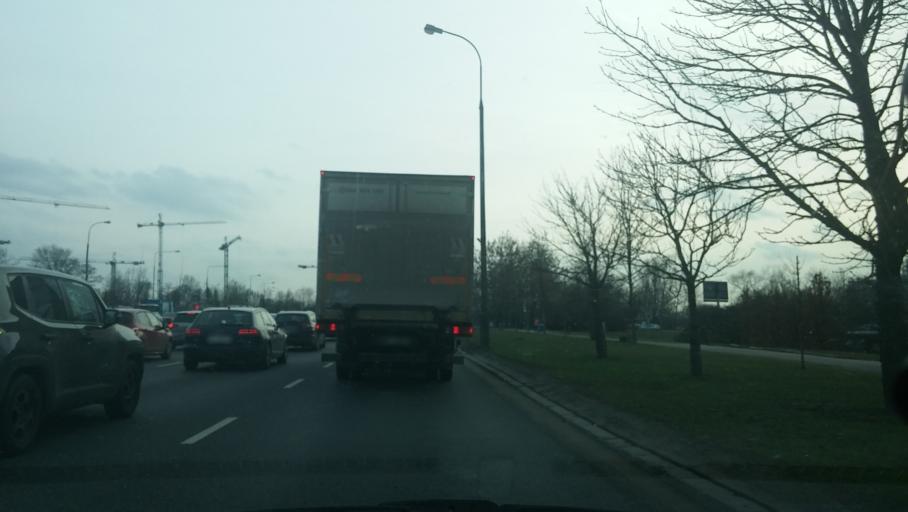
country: PL
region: Masovian Voivodeship
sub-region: Warszawa
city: Mokotow
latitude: 52.1721
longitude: 21.0425
